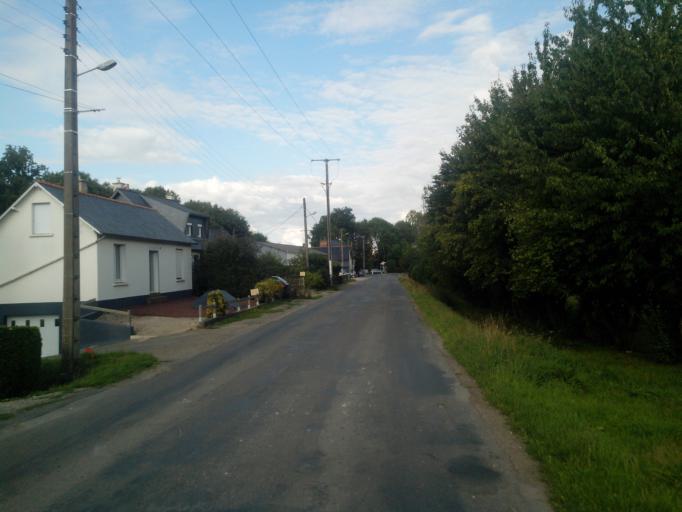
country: FR
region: Brittany
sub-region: Departement d'Ille-et-Vilaine
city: Iffendic
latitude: 48.1256
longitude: -2.0362
